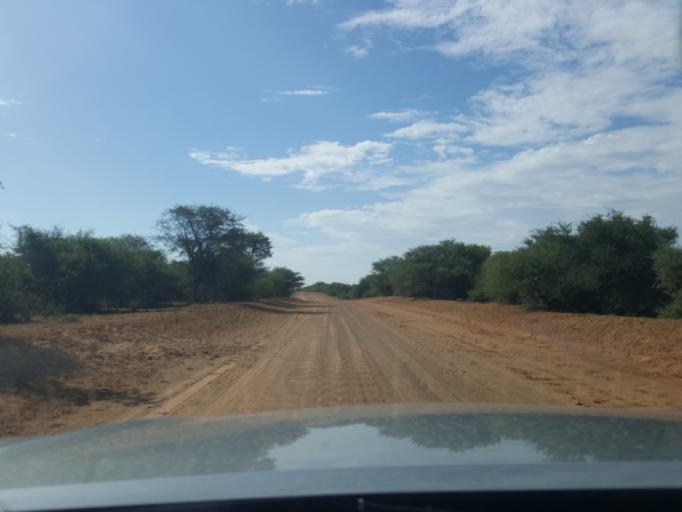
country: BW
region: Kweneng
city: Khudumelapye
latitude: -23.5383
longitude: 24.7281
